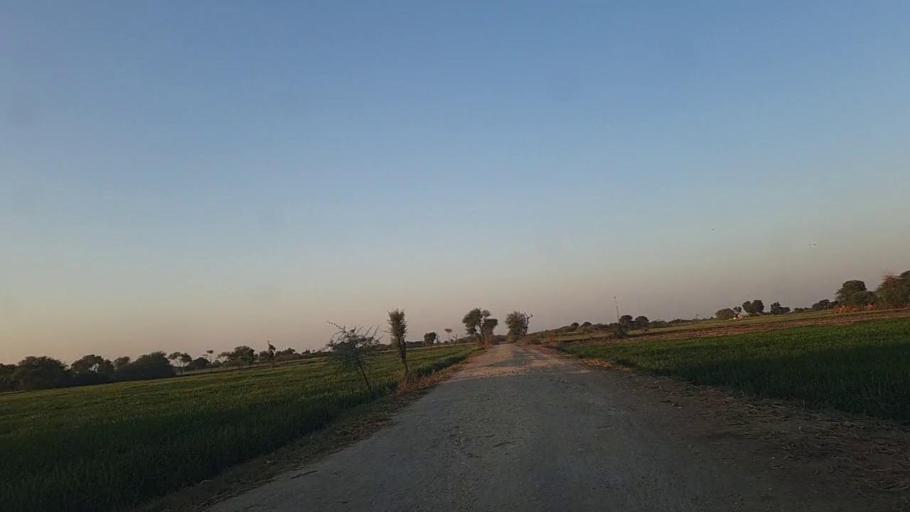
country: PK
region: Sindh
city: Naukot
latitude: 25.0447
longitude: 69.4100
